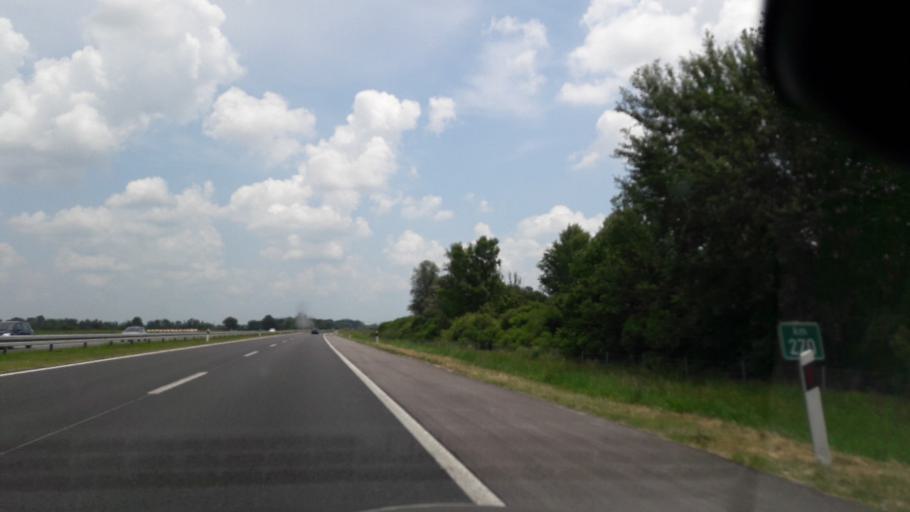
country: HR
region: Vukovarsko-Srijemska
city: Stitar
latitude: 45.1107
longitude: 18.6663
